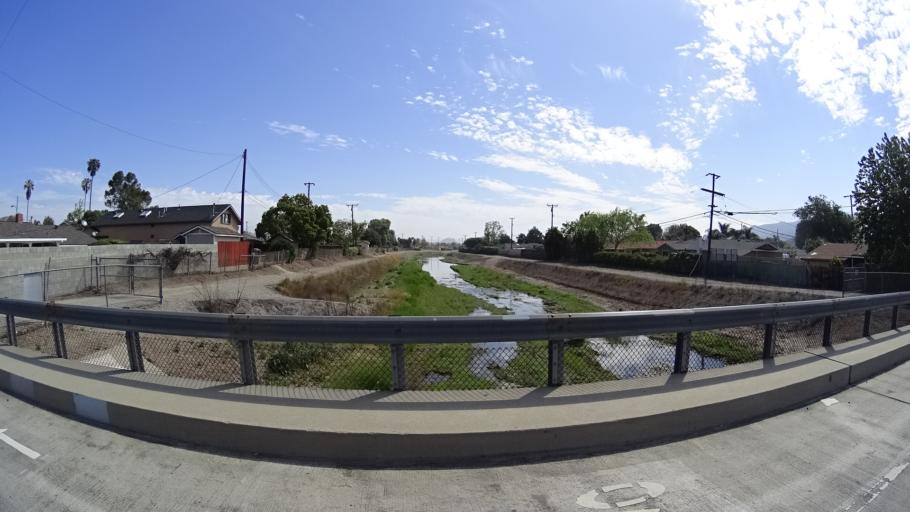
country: US
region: California
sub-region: Ventura County
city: Casa Conejo
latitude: 34.1827
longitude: -118.9441
